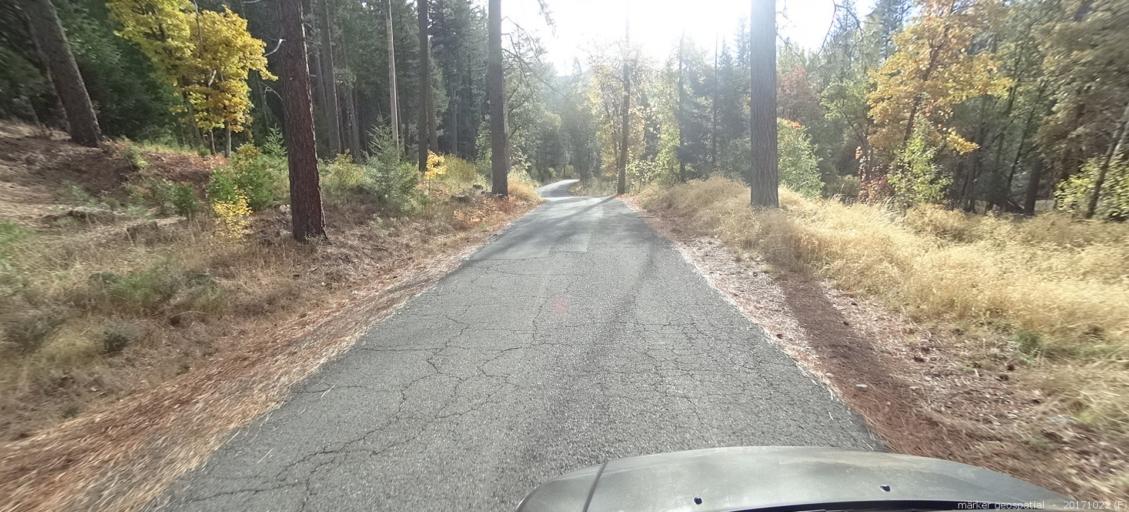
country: US
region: California
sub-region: Siskiyou County
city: Dunsmuir
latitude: 41.1552
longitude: -122.3448
